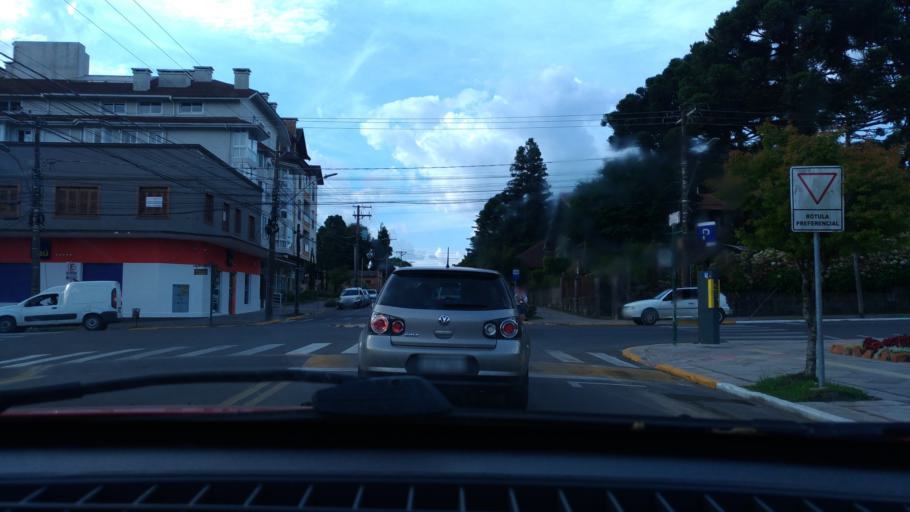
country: BR
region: Rio Grande do Sul
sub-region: Canela
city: Canela
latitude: -29.3633
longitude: -50.8115
